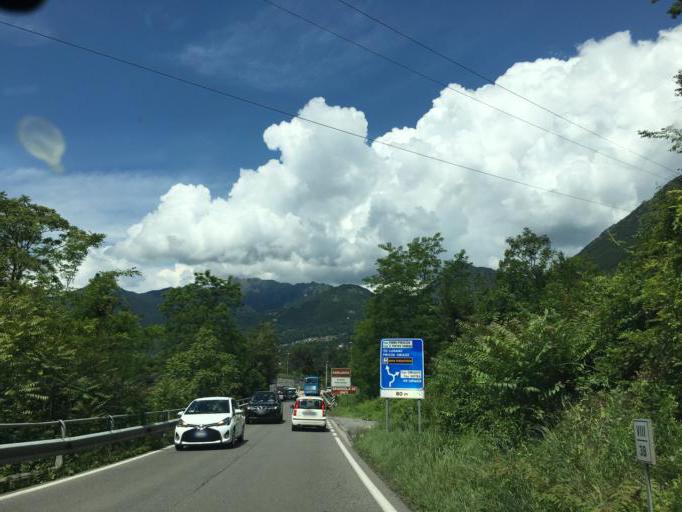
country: IT
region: Lombardy
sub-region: Provincia di Como
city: Bene Lario
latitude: 46.0378
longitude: 9.1803
